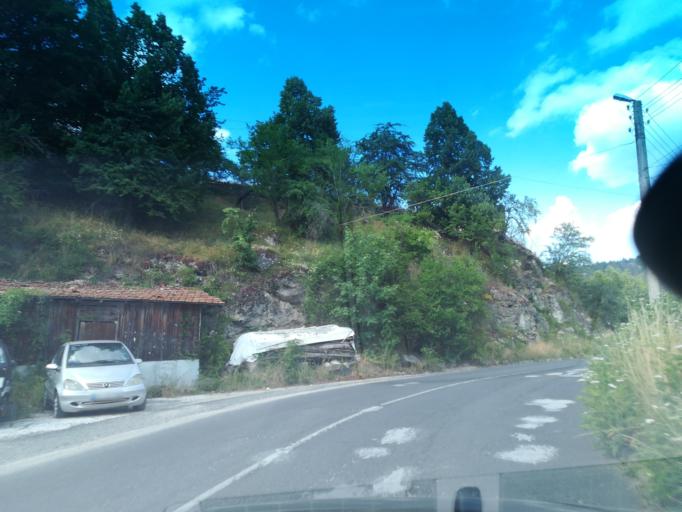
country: BG
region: Smolyan
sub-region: Obshtina Smolyan
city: Smolyan
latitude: 41.6541
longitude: 24.7707
